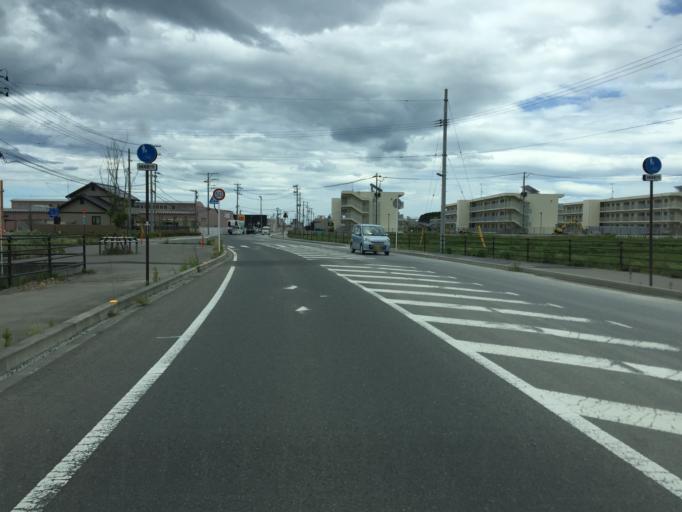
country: JP
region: Fukushima
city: Namie
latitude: 37.6272
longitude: 140.9848
